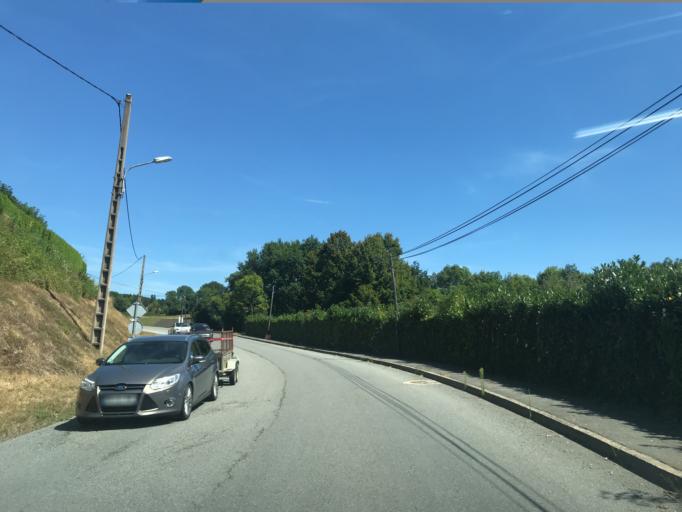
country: FR
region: Limousin
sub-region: Departement de la Creuse
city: Felletin
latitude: 45.8900
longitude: 2.1805
